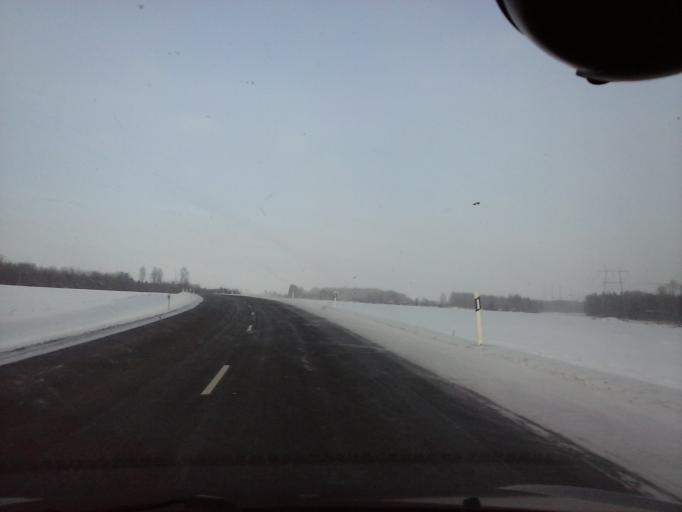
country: EE
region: Viljandimaa
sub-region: Abja vald
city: Abja-Paluoja
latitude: 58.2916
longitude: 25.2961
